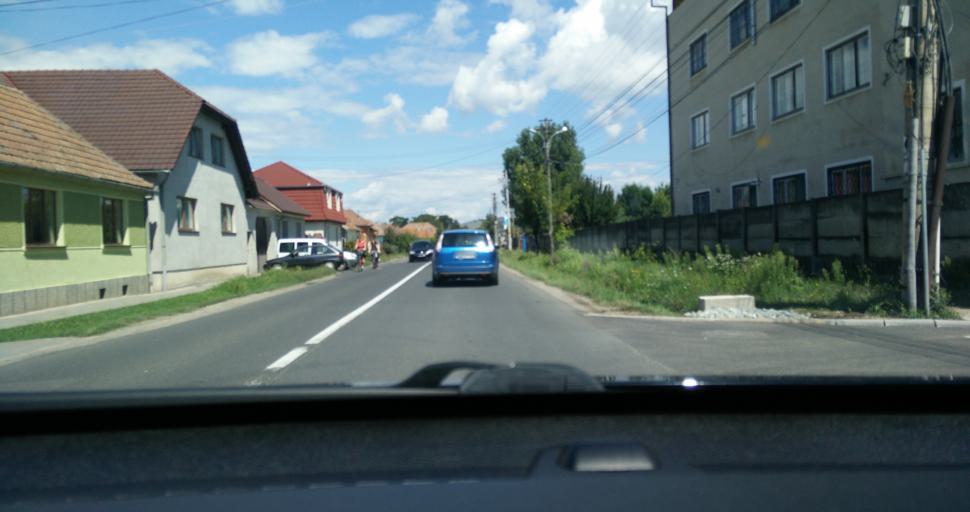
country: RO
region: Alba
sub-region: Municipiul Sebes
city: Sebes
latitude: 45.9451
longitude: 23.5641
